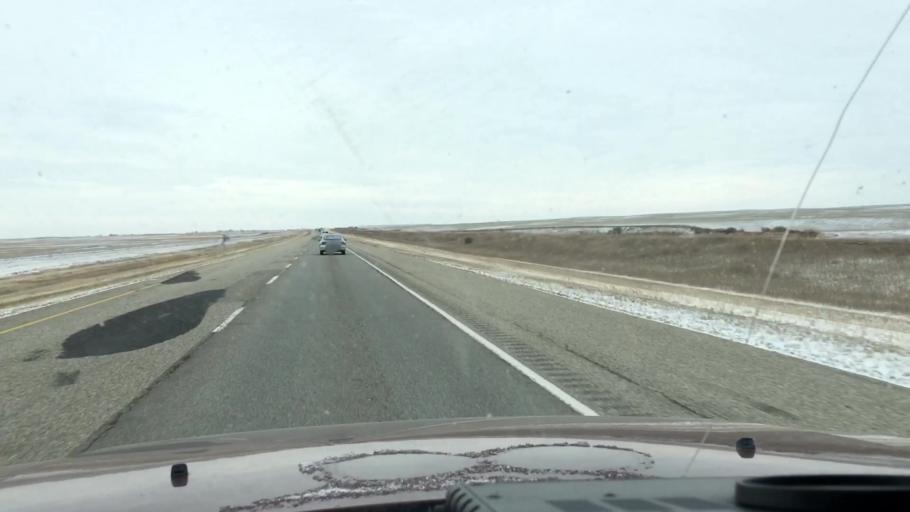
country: CA
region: Saskatchewan
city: Saskatoon
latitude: 51.4631
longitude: -106.2374
